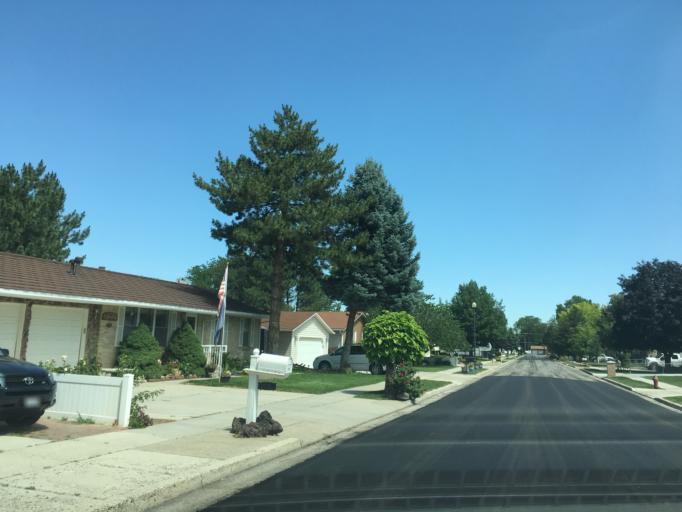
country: US
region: Utah
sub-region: Salt Lake County
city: Sandy City
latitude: 40.5924
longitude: -111.8656
